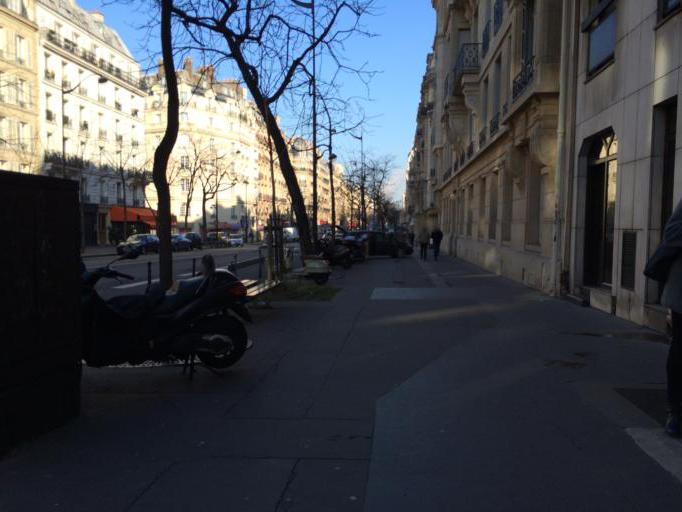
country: FR
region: Ile-de-France
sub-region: Departement des Hauts-de-Seine
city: Levallois-Perret
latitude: 48.8797
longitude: 2.2994
